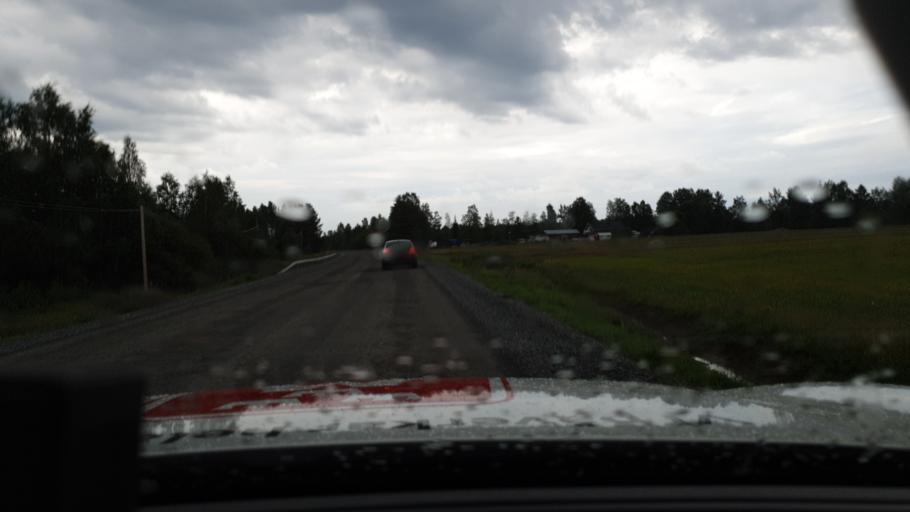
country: SE
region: Norrbotten
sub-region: Bodens Kommun
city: Boden
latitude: 65.8545
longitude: 21.4824
